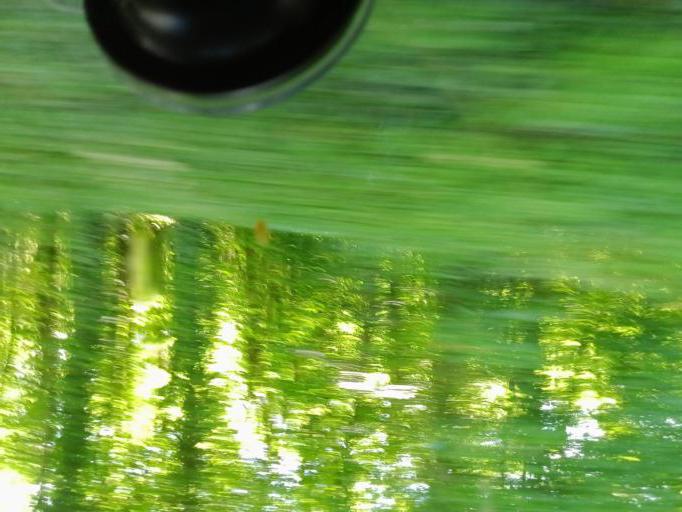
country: IE
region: Leinster
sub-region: Kilkenny
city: Thomastown
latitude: 52.5537
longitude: -7.0929
